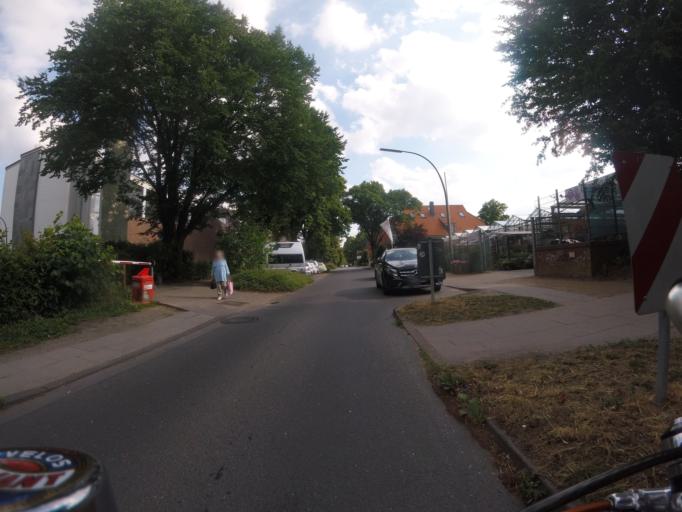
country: DE
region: Hamburg
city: Stellingen
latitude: 53.6206
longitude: 9.9491
